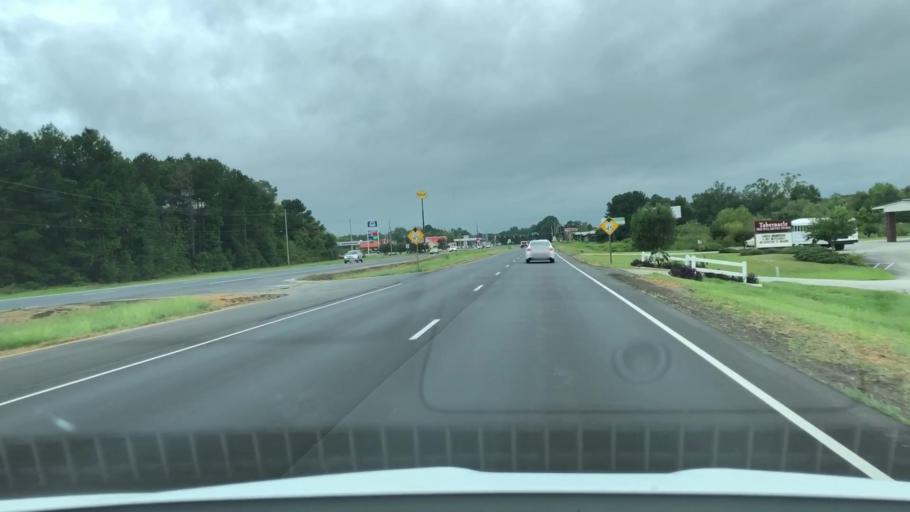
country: US
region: North Carolina
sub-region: Lenoir County
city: Kinston
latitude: 35.2510
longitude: -77.5973
